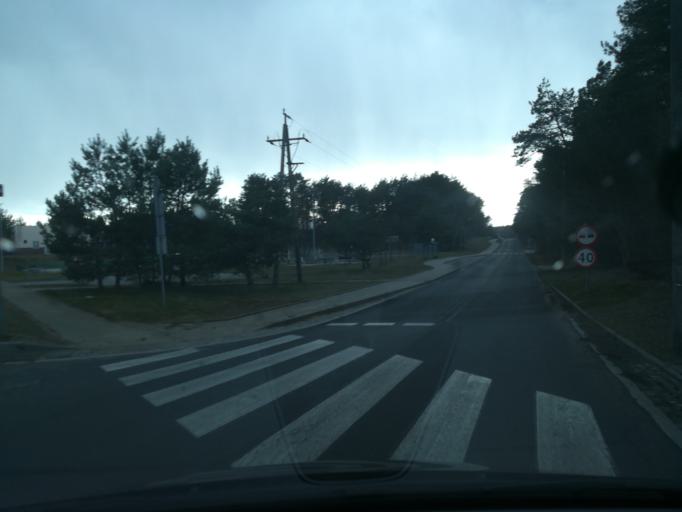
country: PL
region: Kujawsko-Pomorskie
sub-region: Powiat torunski
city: Lubicz Dolny
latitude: 52.9783
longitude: 18.6848
